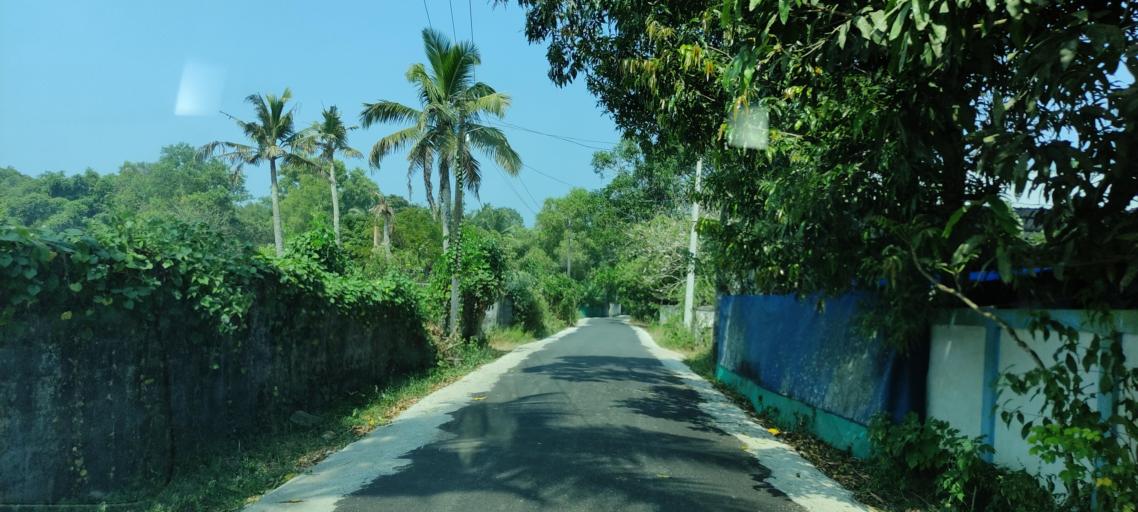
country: IN
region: Kerala
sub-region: Alappuzha
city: Alleppey
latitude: 9.5435
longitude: 76.3203
